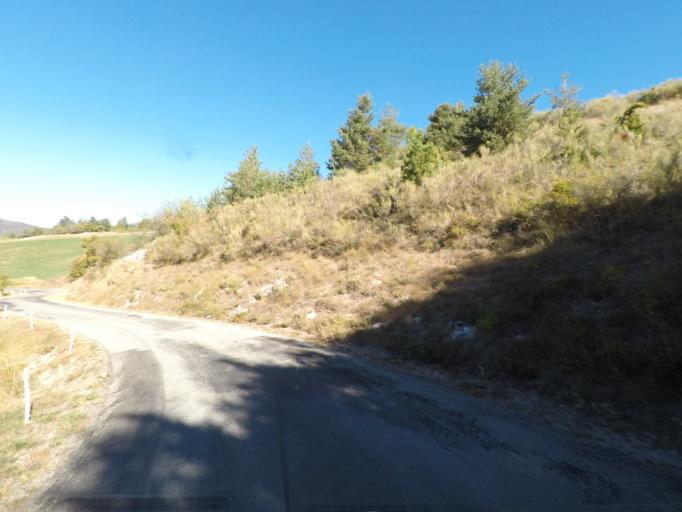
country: FR
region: Rhone-Alpes
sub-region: Departement de la Drome
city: Die
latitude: 44.5478
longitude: 5.3685
